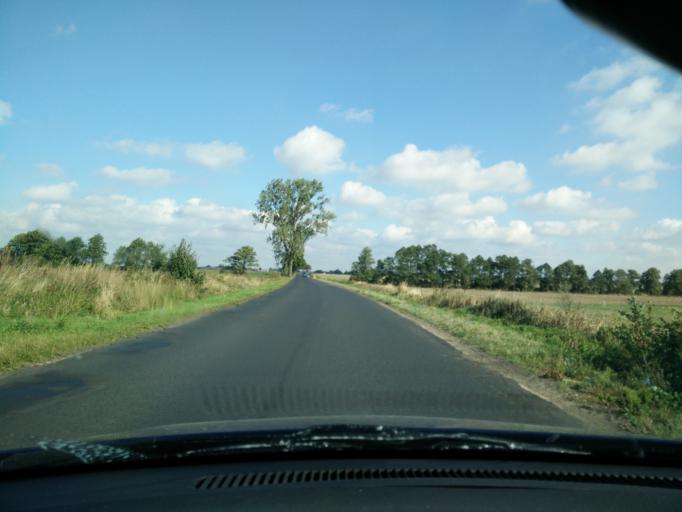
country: PL
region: Greater Poland Voivodeship
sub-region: Powiat sredzki
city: Dominowo
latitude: 52.2756
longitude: 17.3188
